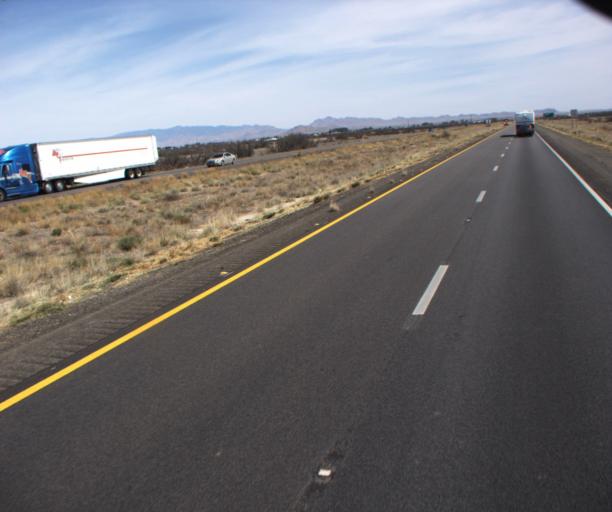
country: US
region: Arizona
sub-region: Cochise County
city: Willcox
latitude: 32.2321
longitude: -109.8704
